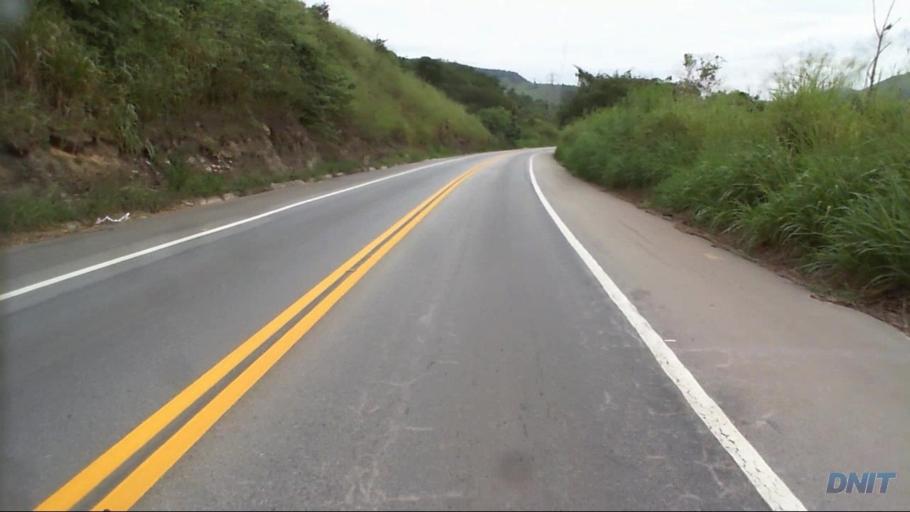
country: BR
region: Minas Gerais
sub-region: Timoteo
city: Timoteo
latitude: -19.5906
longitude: -42.7363
